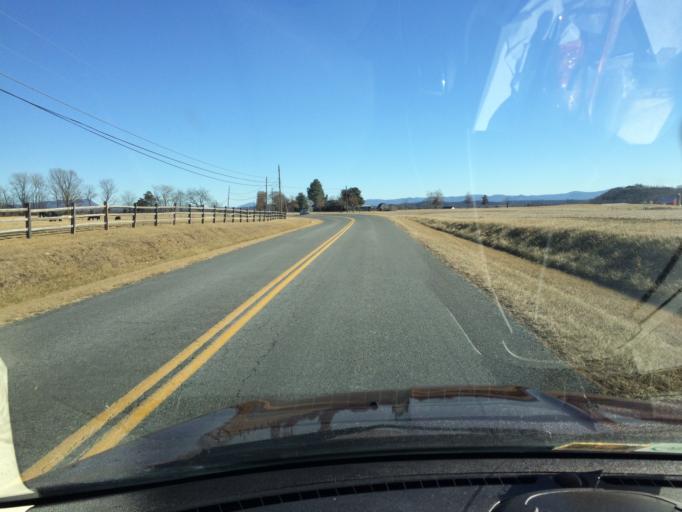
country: US
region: Virginia
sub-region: Rockingham County
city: Bridgewater
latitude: 38.3662
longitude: -78.9747
